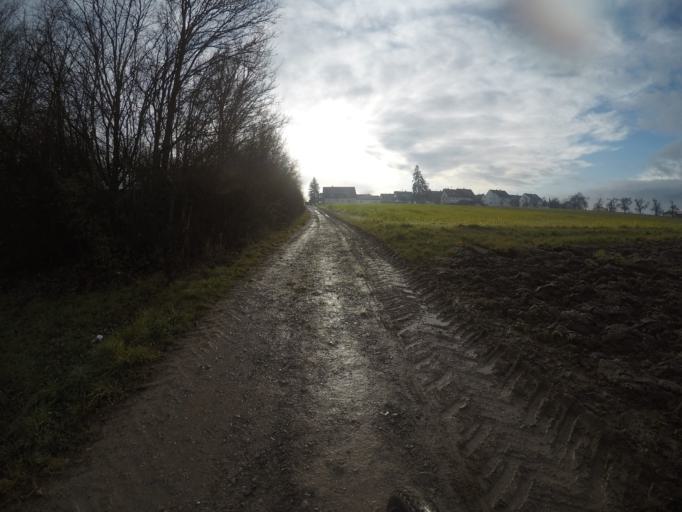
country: DE
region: Baden-Wuerttemberg
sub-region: Regierungsbezirk Stuttgart
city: Herrenberg
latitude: 48.6156
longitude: 8.8372
